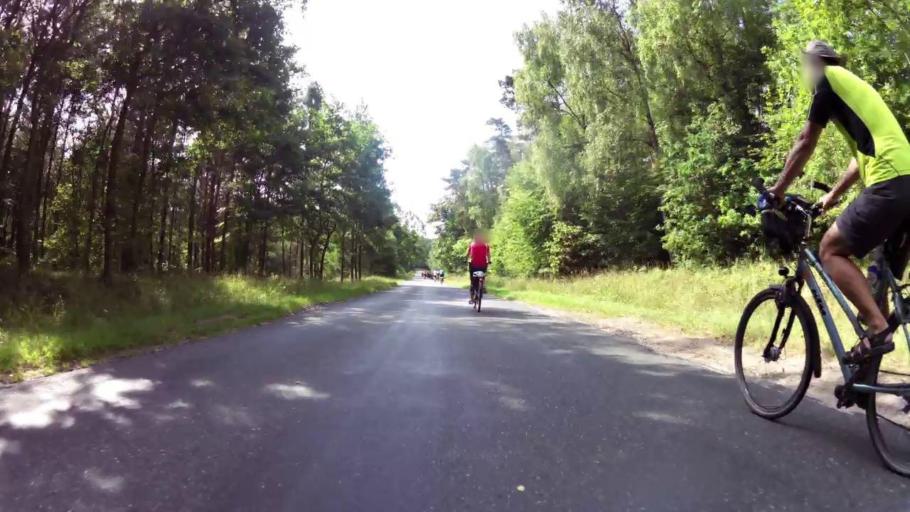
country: PL
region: West Pomeranian Voivodeship
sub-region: Powiat drawski
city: Drawsko Pomorskie
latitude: 53.4805
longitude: 15.7765
